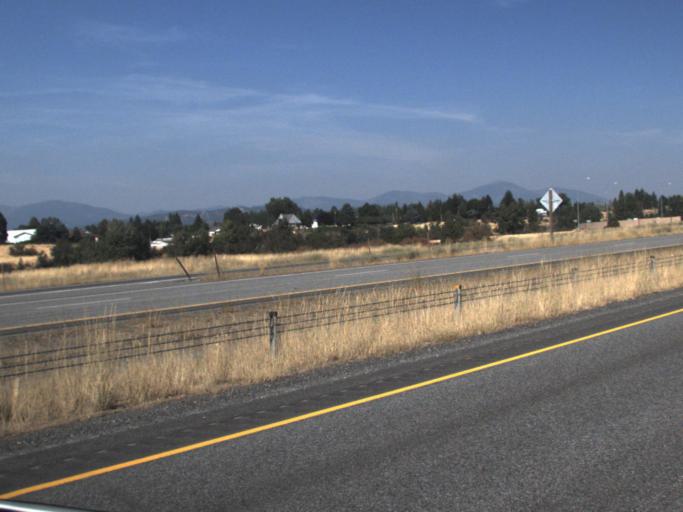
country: US
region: Washington
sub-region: Spokane County
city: Otis Orchards-East Farms
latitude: 47.6855
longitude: -117.0759
